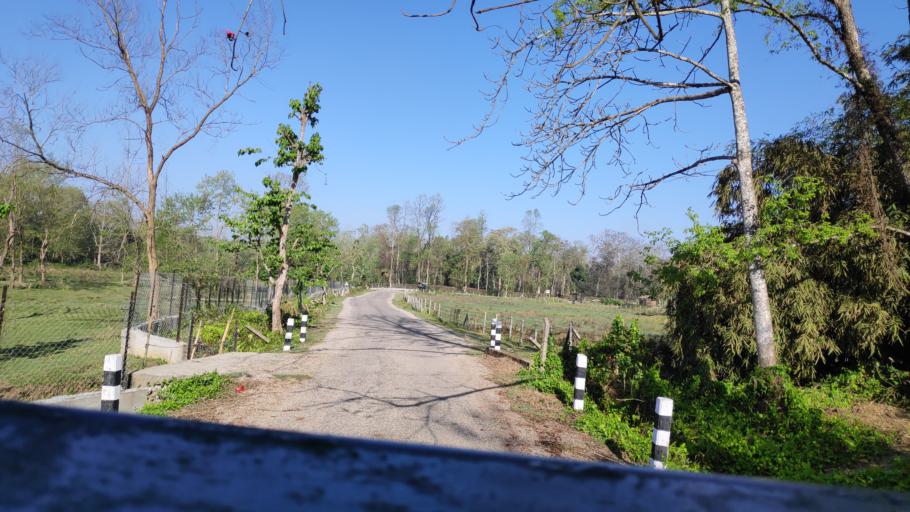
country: NP
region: Central Region
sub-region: Narayani Zone
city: Bharatpur
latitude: 27.5691
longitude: 84.5188
